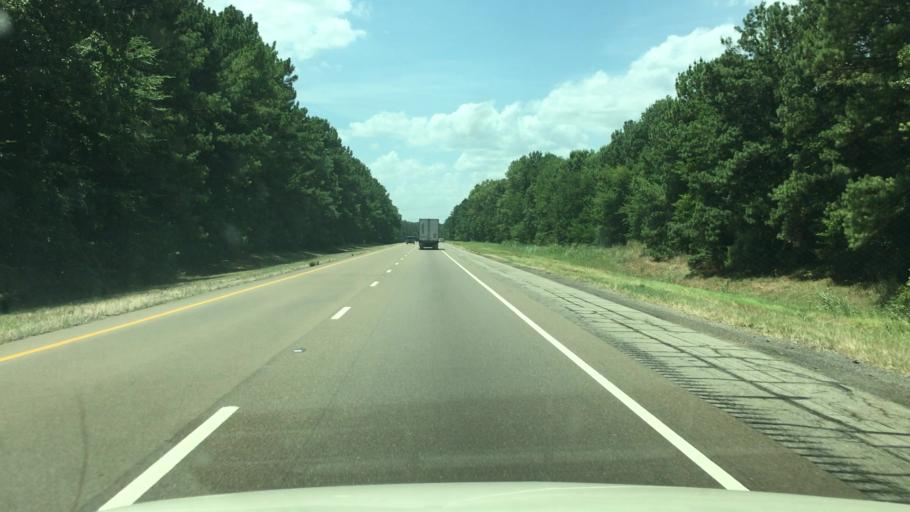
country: US
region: Texas
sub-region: Morris County
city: Naples
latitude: 33.3074
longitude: -94.7025
